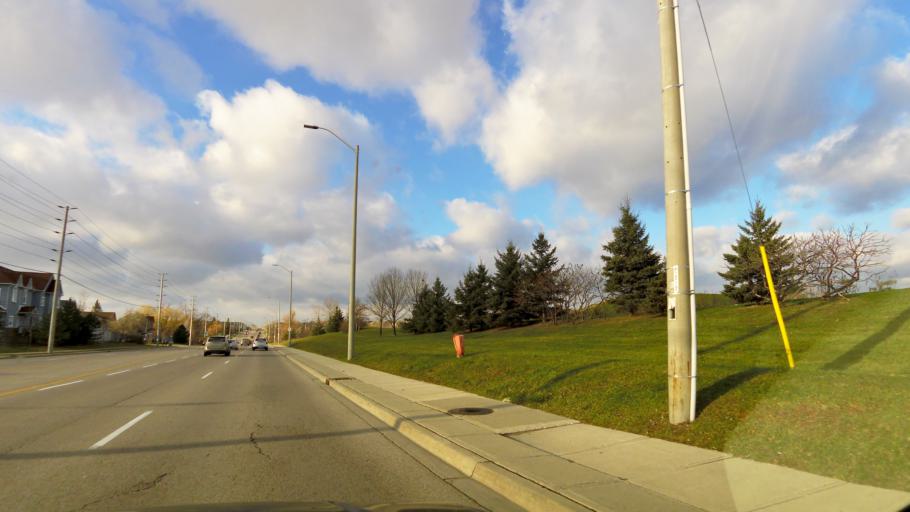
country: CA
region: Ontario
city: Mississauga
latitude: 43.6275
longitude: -79.7044
